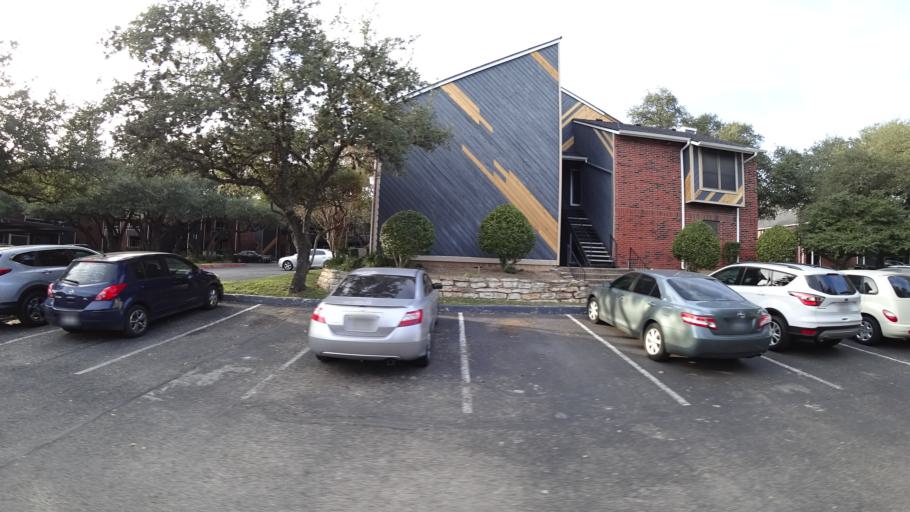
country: US
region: Texas
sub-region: Williamson County
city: Jollyville
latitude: 30.3920
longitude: -97.7553
